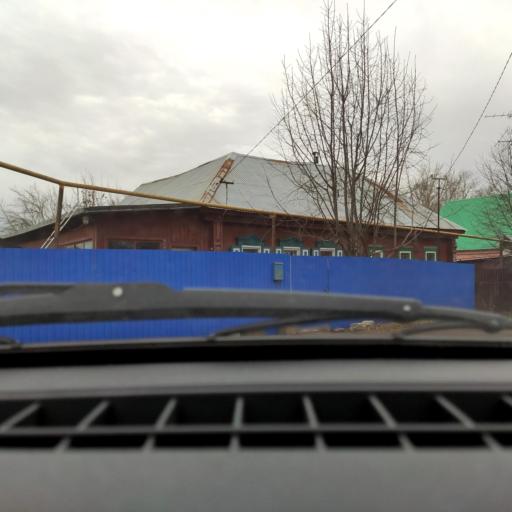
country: RU
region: Bashkortostan
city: Ufa
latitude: 54.8290
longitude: 56.0726
